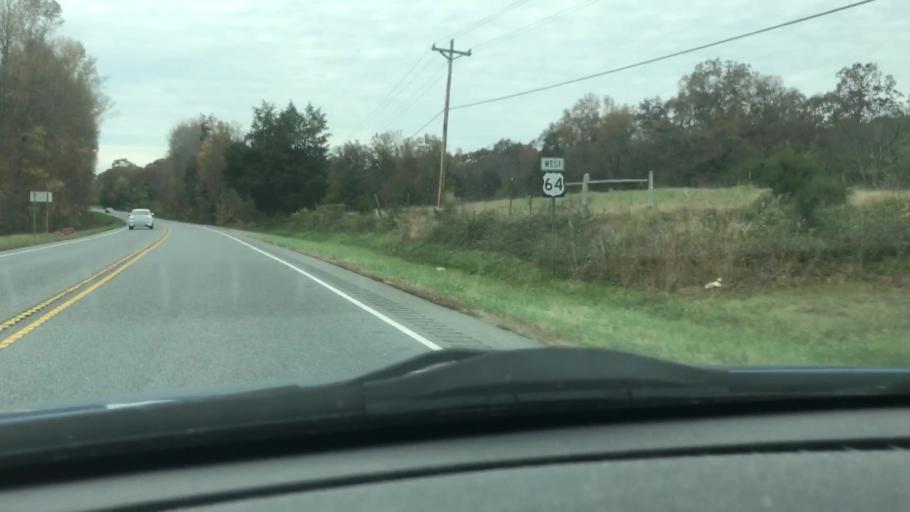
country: US
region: North Carolina
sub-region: Randolph County
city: Asheboro
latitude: 35.7315
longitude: -79.9447
